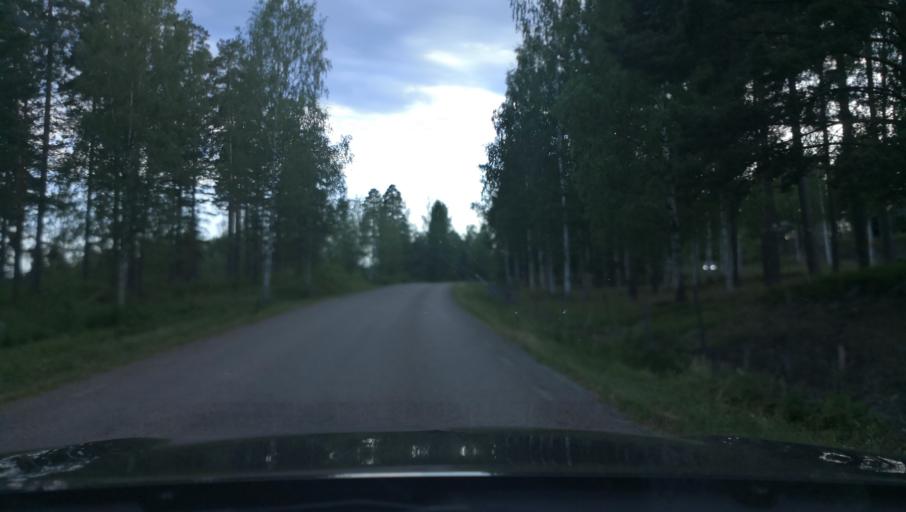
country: SE
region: Dalarna
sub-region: Ludvika Kommun
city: Ludvika
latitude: 60.1177
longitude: 15.2588
